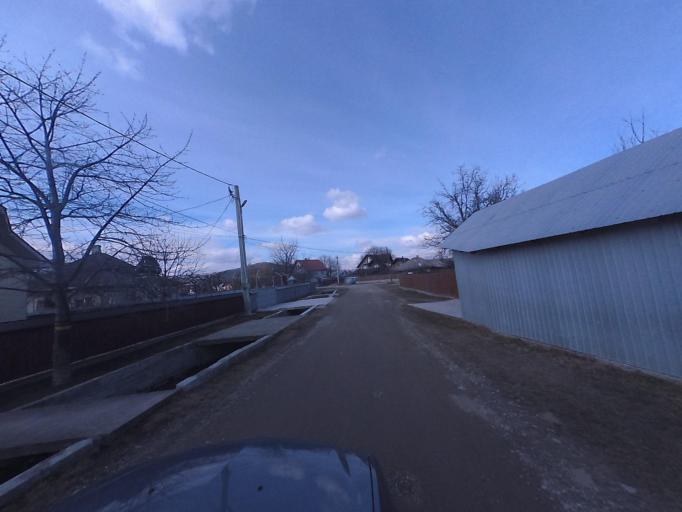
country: RO
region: Neamt
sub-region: Oras Targu Neamt
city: Targu Neamt
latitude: 47.2050
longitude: 26.3828
